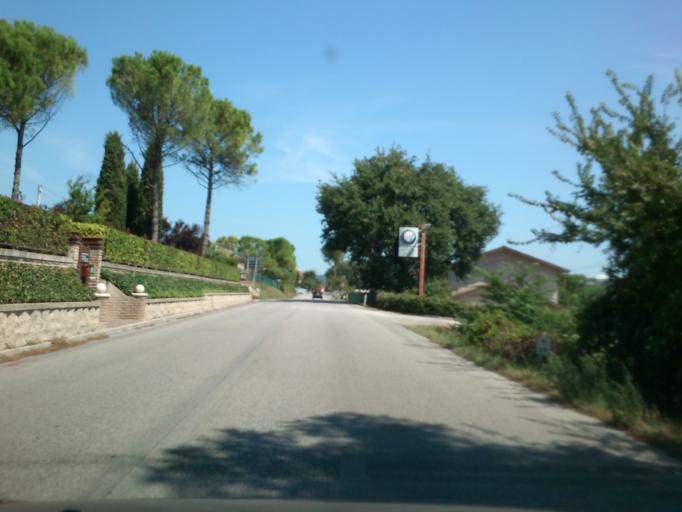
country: IT
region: The Marches
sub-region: Provincia di Pesaro e Urbino
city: Lucrezia
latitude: 43.7669
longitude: 12.9307
